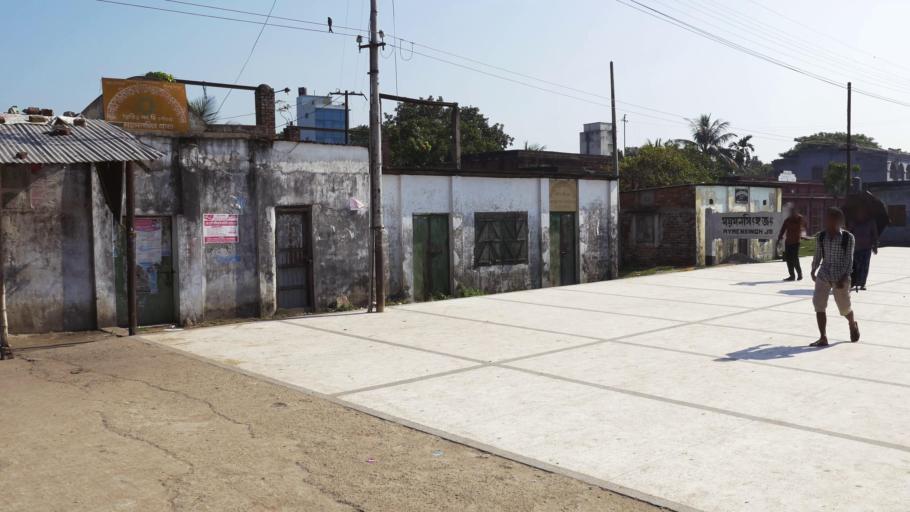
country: BD
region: Dhaka
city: Mymensingh
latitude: 24.6775
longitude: 90.4545
